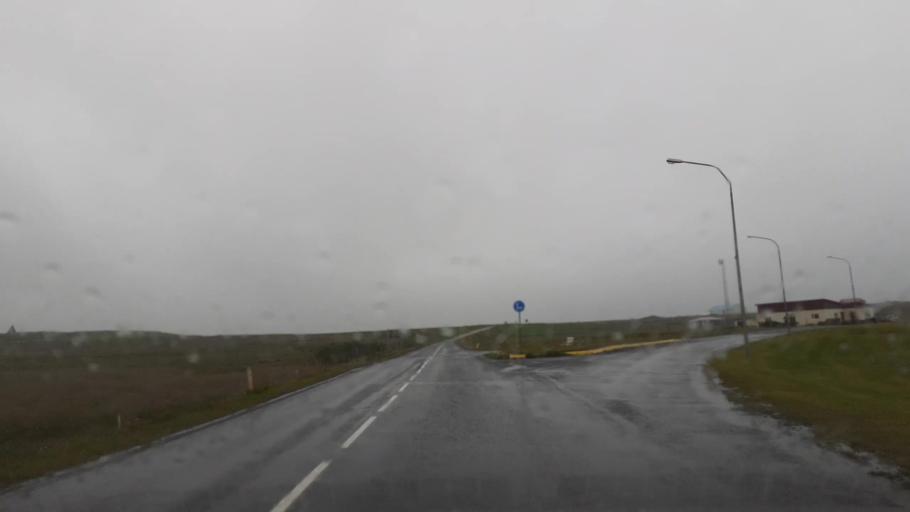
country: IS
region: Northeast
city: Husavik
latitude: 66.4567
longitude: -15.9512
